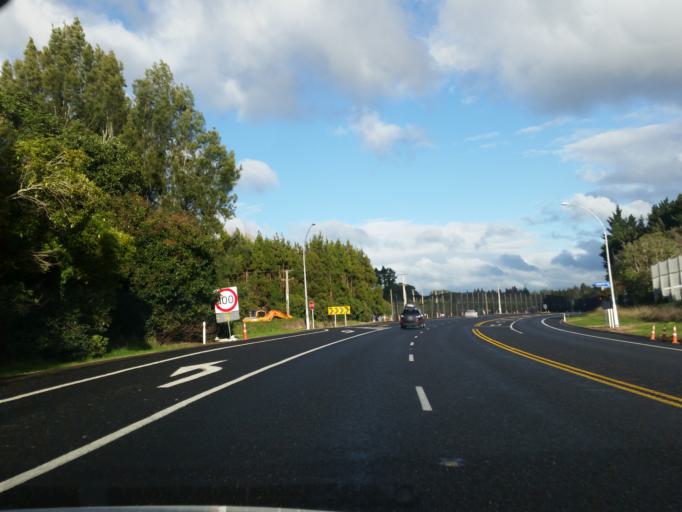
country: NZ
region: Bay of Plenty
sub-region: Western Bay of Plenty District
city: Katikati
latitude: -37.6161
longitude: 175.9503
